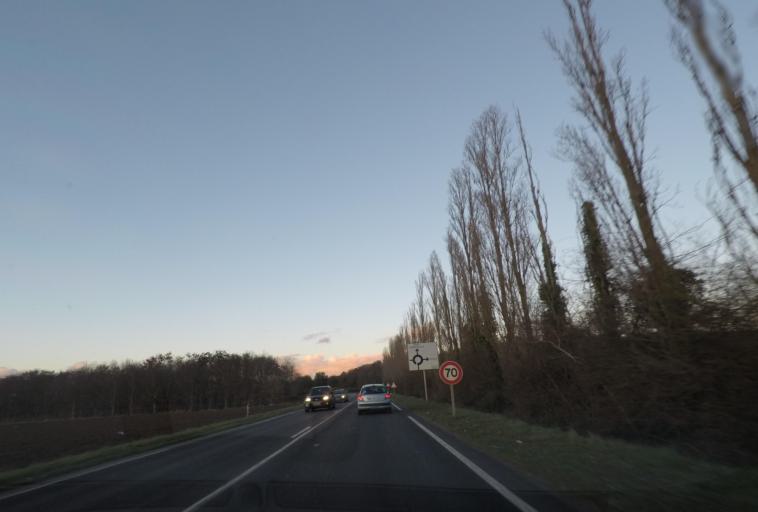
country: FR
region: Ile-de-France
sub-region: Departement de l'Essonne
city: Bondoufle
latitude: 48.5932
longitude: 2.3709
